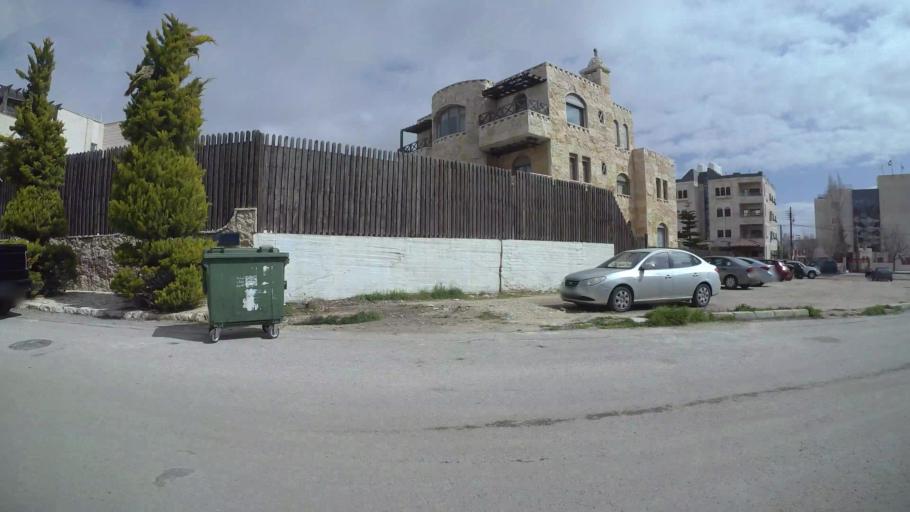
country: JO
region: Amman
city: Al Jubayhah
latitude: 31.9995
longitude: 35.8349
